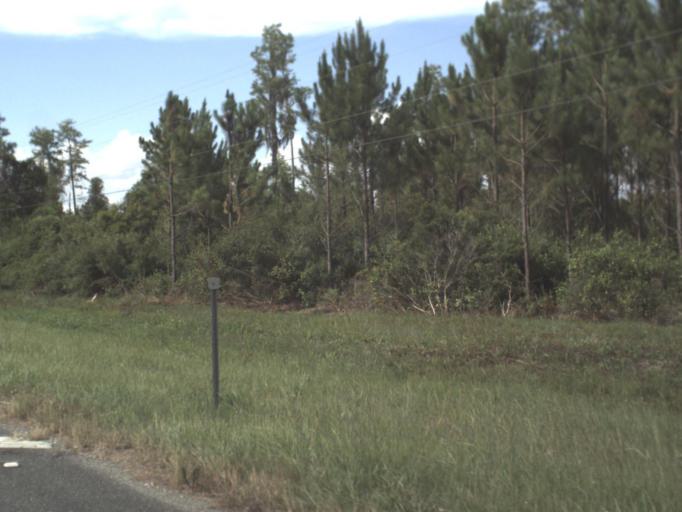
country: US
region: Florida
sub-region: Taylor County
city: Perry
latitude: 30.2141
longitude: -83.6127
